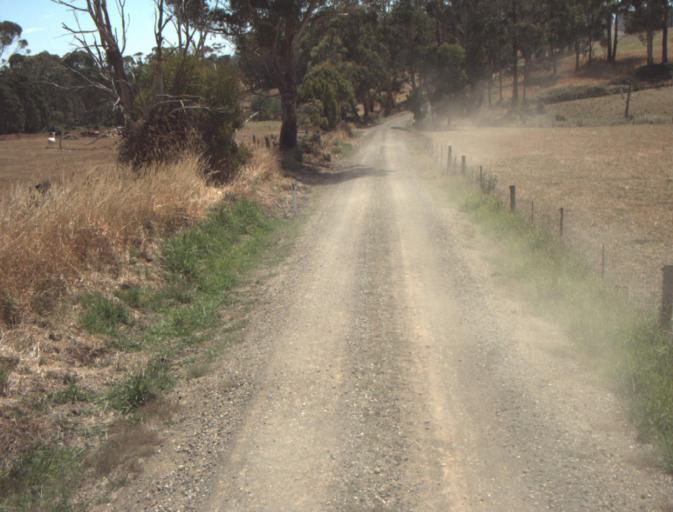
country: AU
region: Tasmania
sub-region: Launceston
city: Mayfield
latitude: -41.2648
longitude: 147.1491
